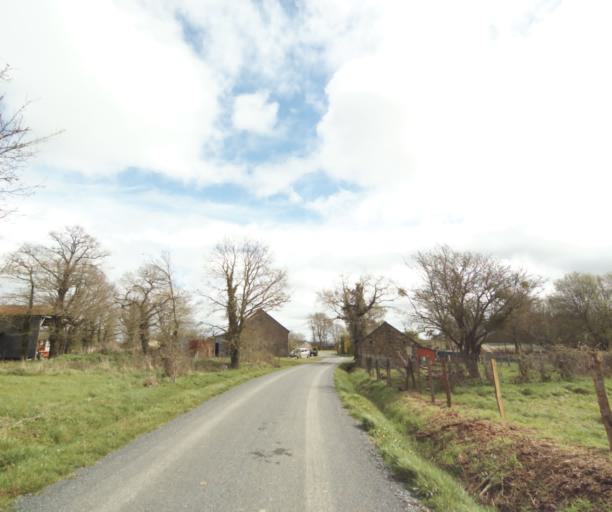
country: FR
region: Pays de la Loire
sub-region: Departement de la Loire-Atlantique
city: Bouvron
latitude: 47.4354
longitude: -1.8524
